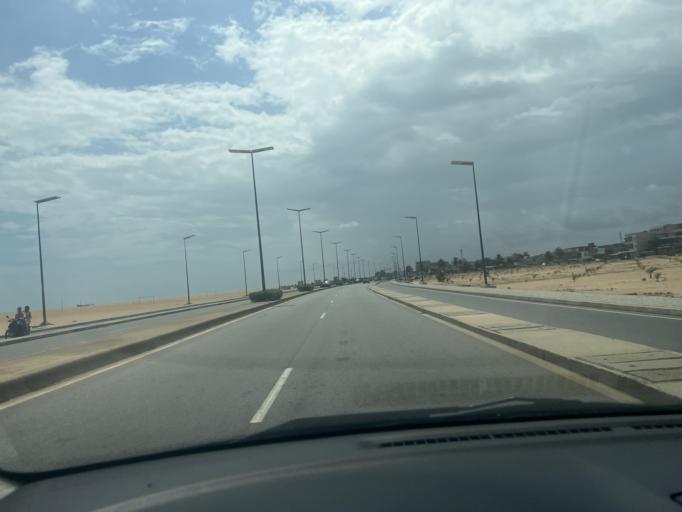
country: BJ
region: Littoral
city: Cotonou
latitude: 6.3489
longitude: 2.3692
